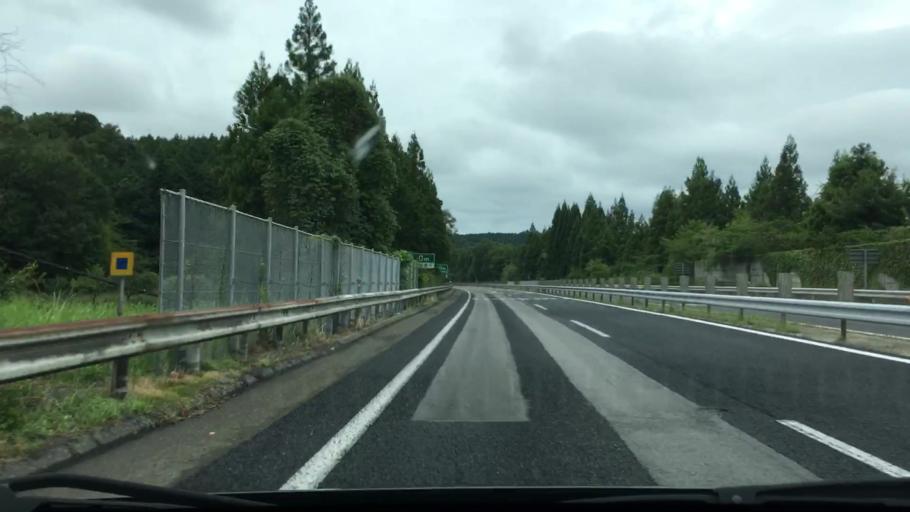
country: JP
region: Hiroshima
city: Miyoshi
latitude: 34.7985
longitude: 132.8963
